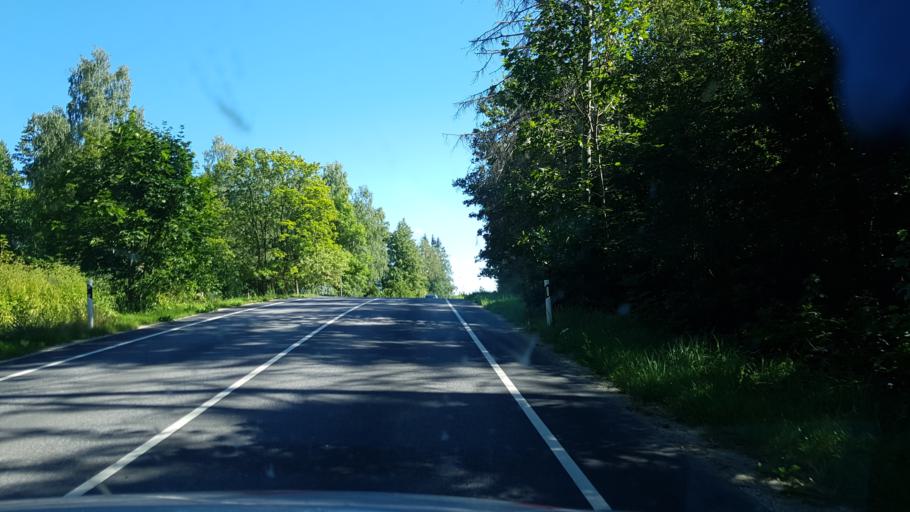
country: EE
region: Jaervamaa
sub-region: Jaerva-Jaani vald
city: Jarva-Jaani
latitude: 59.0301
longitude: 25.8943
